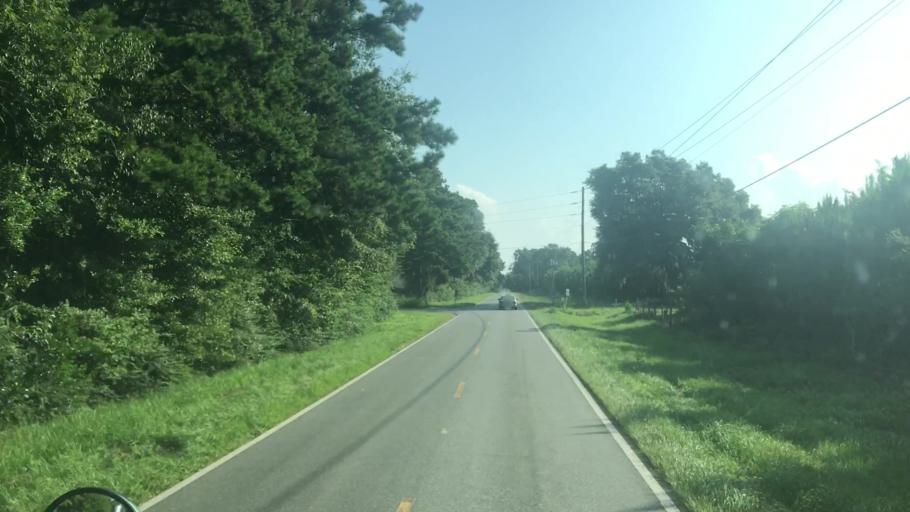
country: US
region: Florida
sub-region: Gadsden County
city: Quincy
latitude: 30.6404
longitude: -84.5748
